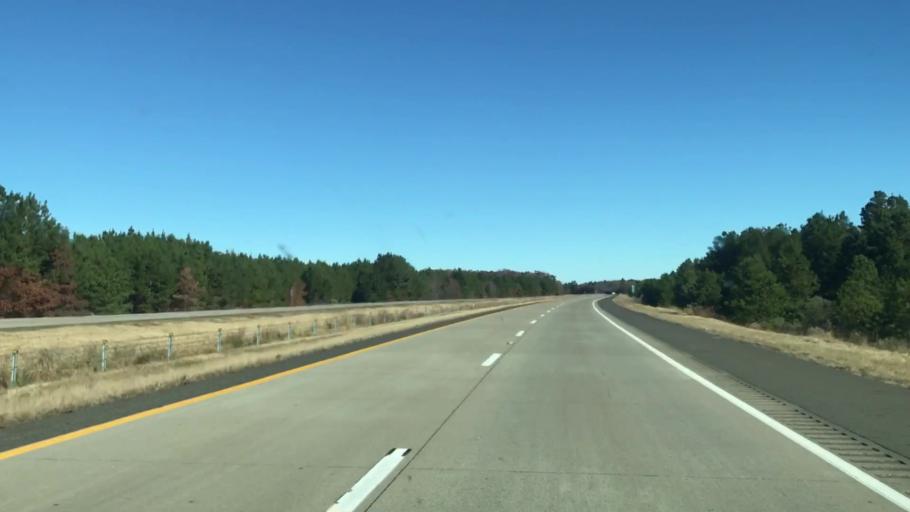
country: US
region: Texas
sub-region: Cass County
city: Queen City
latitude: 33.2025
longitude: -93.8767
